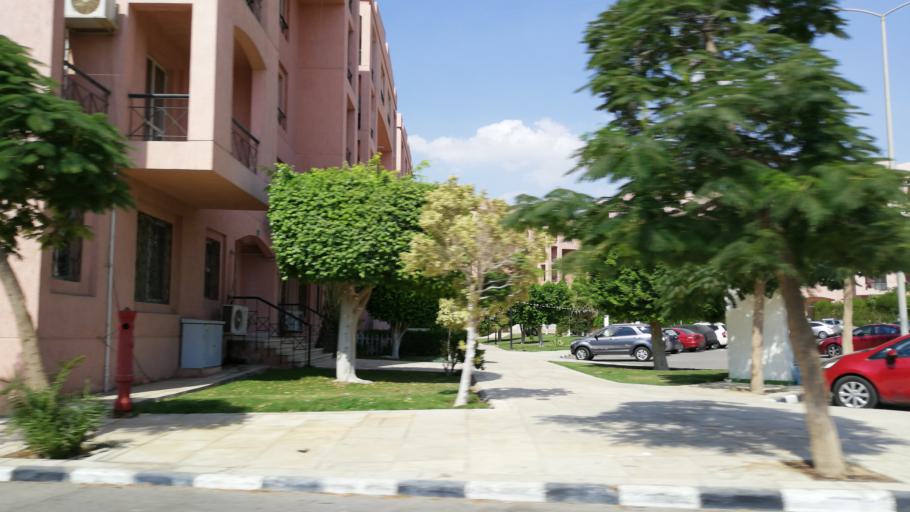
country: EG
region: Muhafazat al Qalyubiyah
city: Al Khankah
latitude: 30.0627
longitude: 31.4877
